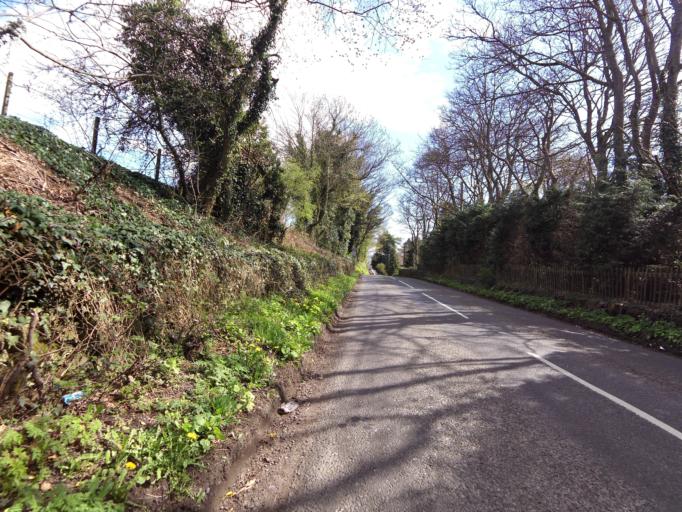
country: GB
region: Scotland
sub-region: Fife
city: Auchtermuchty
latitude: 56.2986
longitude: -3.2391
